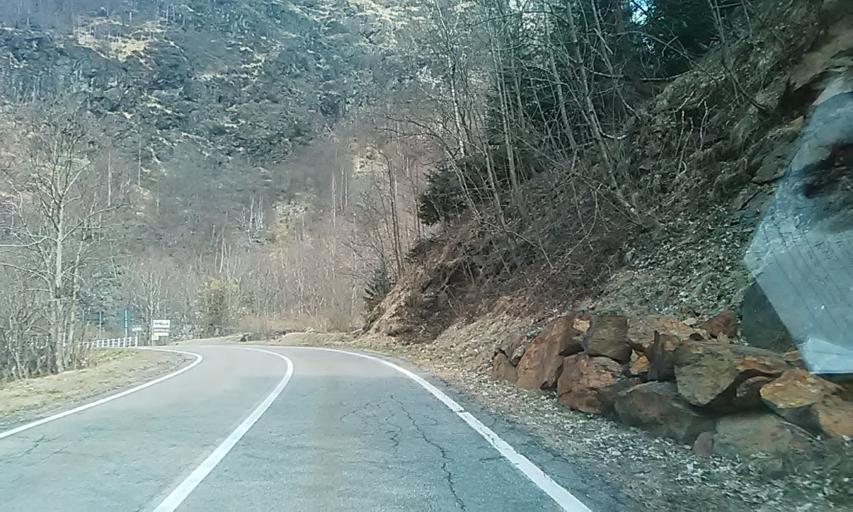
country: IT
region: Piedmont
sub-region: Provincia di Vercelli
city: Rimella
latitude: 45.8982
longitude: 8.1825
